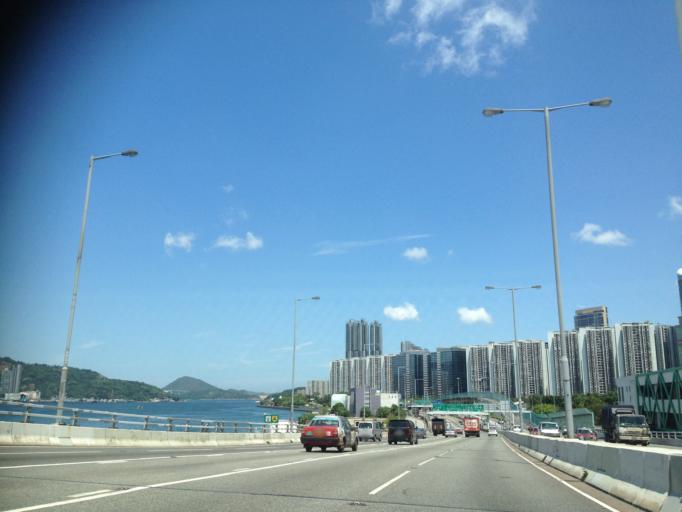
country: HK
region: Kowloon City
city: Kowloon
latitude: 22.2925
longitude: 114.2097
